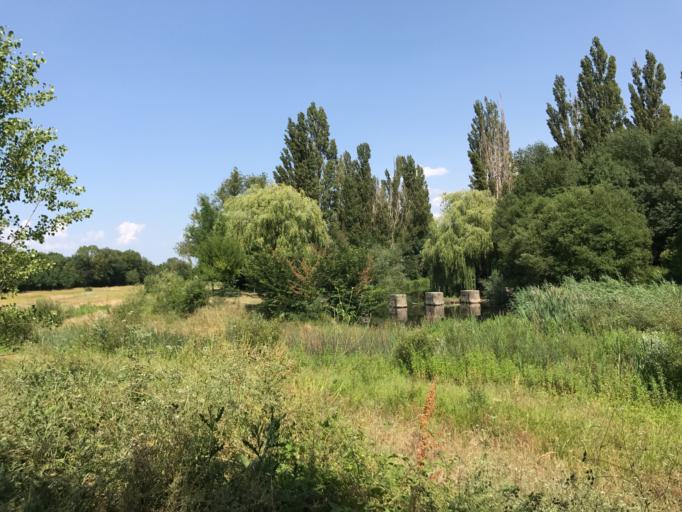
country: ES
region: Basque Country
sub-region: Provincia de Alava
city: Gasteiz / Vitoria
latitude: 42.8770
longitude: -2.6554
